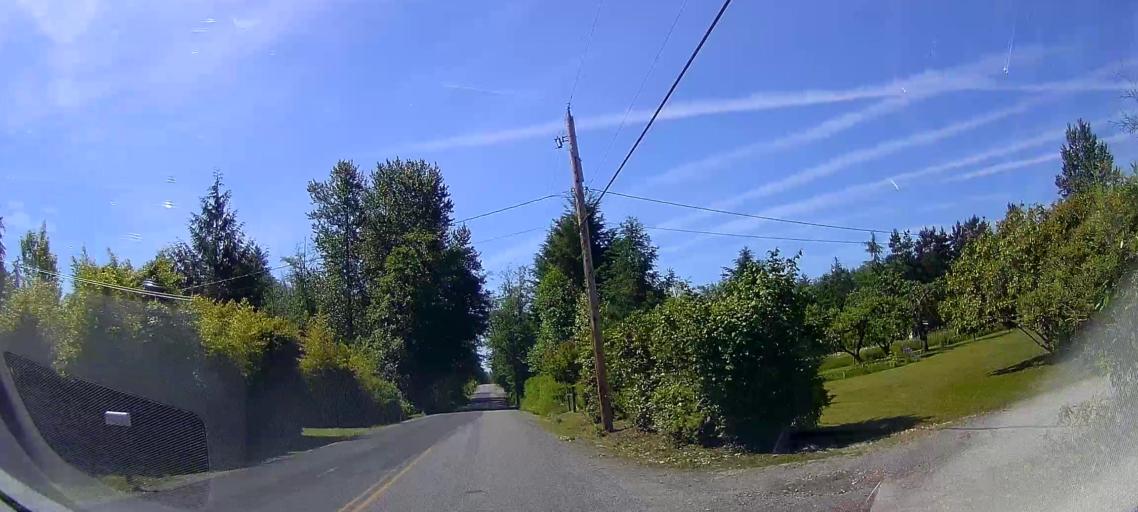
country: US
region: Washington
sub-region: Skagit County
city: Sedro-Woolley
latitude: 48.5498
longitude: -122.2475
